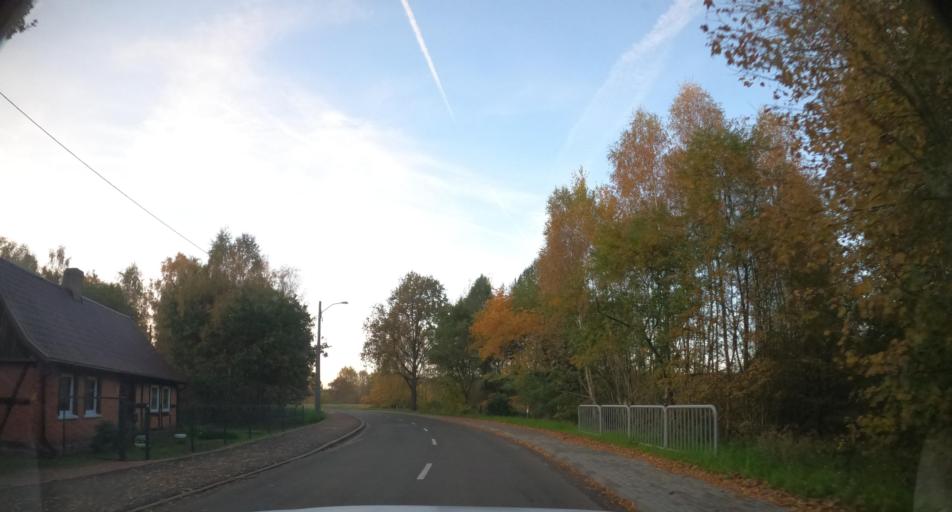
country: PL
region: West Pomeranian Voivodeship
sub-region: Powiat policki
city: Police
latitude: 53.6562
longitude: 14.4947
